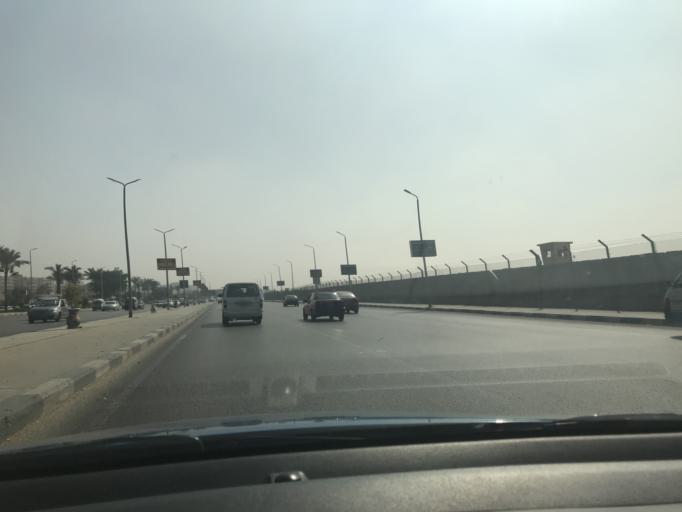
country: EG
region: Muhafazat al Qalyubiyah
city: Al Khankah
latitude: 30.1347
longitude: 31.3900
